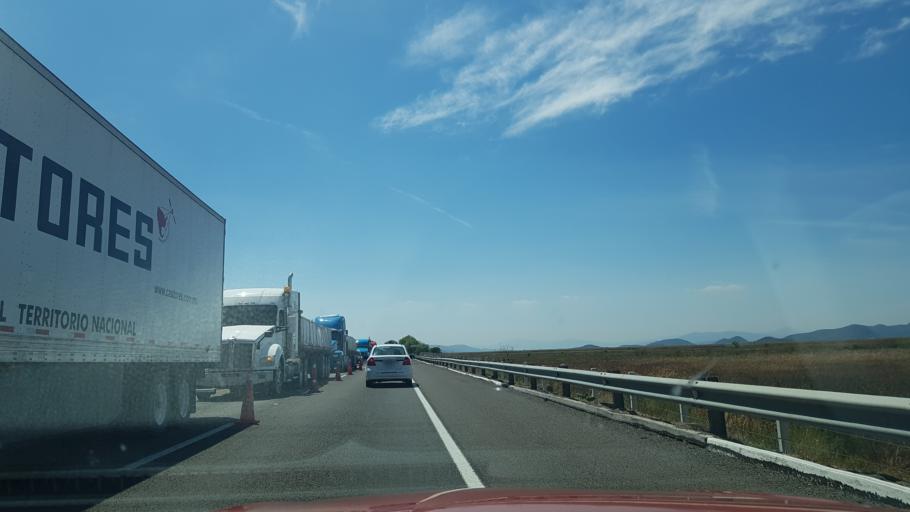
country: MX
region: Michoacan
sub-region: Zinapecuaro
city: Jose Maria Morelos (La Yegueeria)
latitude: 19.8999
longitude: -100.8735
